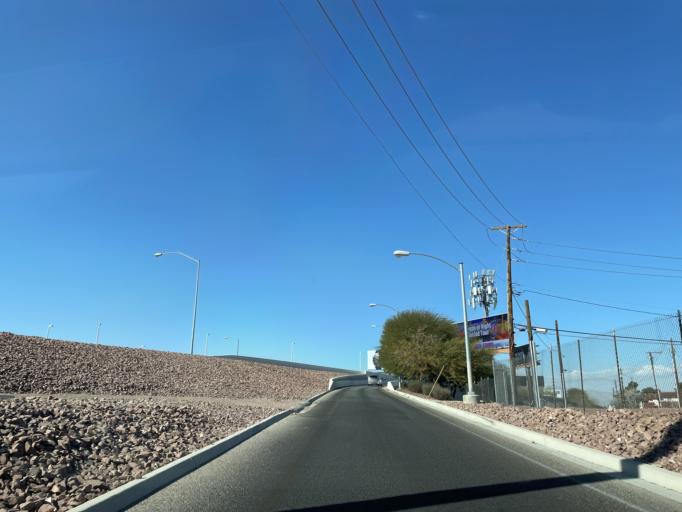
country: US
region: Nevada
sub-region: Clark County
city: Paradise
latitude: 36.0902
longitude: -115.1457
